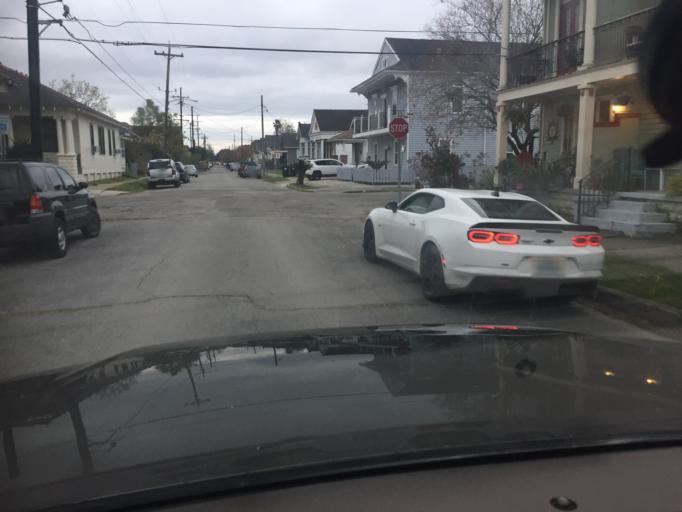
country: US
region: Louisiana
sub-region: Orleans Parish
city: New Orleans
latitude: 29.9763
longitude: -90.0856
